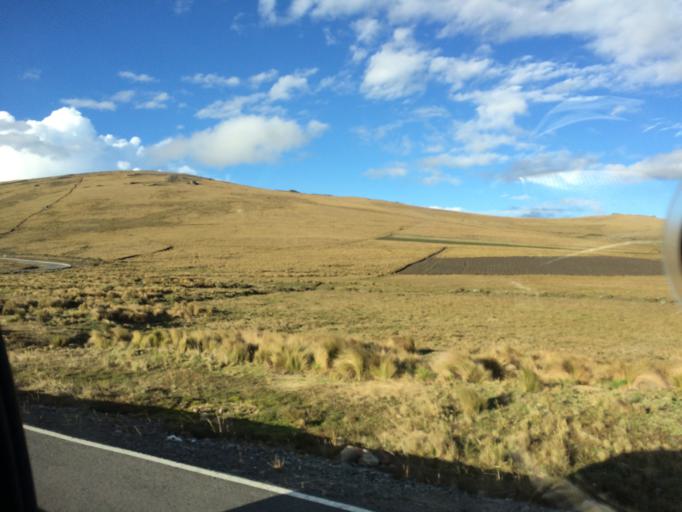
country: EC
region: Chimborazo
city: Alausi
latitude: -2.2273
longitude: -78.6870
